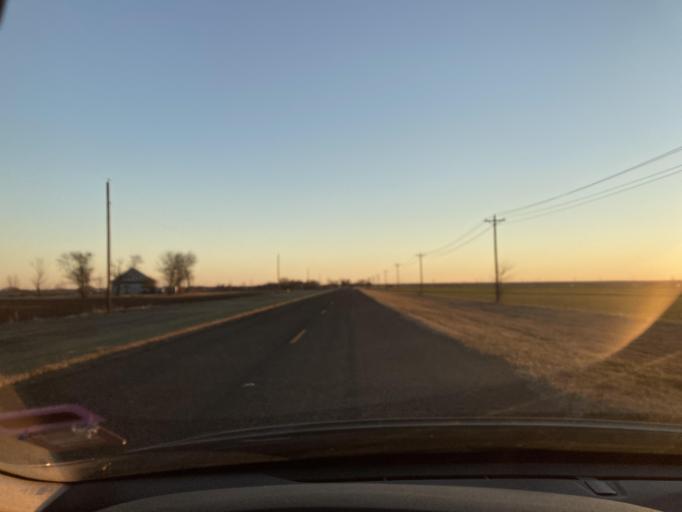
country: US
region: Texas
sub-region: Ellis County
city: Nash
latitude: 32.2859
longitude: -96.8980
